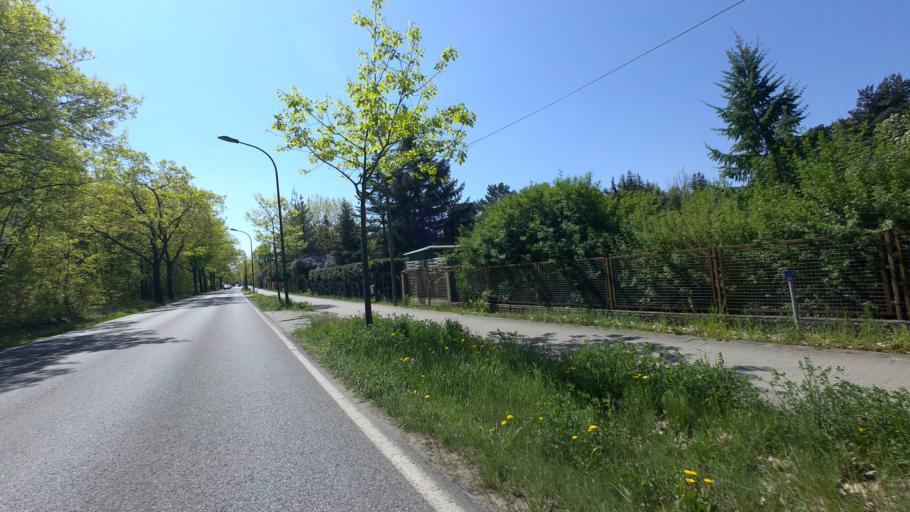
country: DE
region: Brandenburg
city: Bestensee
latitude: 52.2670
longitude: 13.6342
